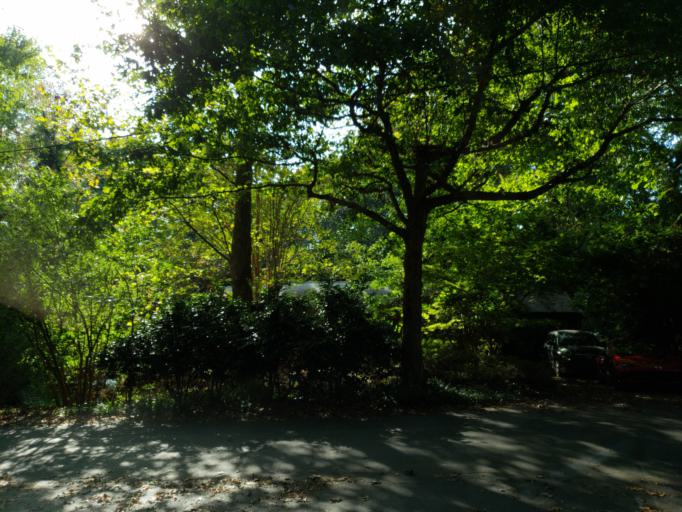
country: US
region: Georgia
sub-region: Fulton County
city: Roswell
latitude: 34.0810
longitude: -84.4118
